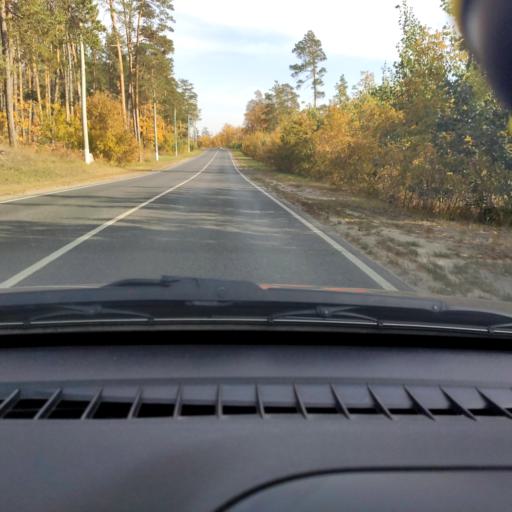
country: RU
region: Samara
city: Tol'yatti
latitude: 53.4734
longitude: 49.3833
